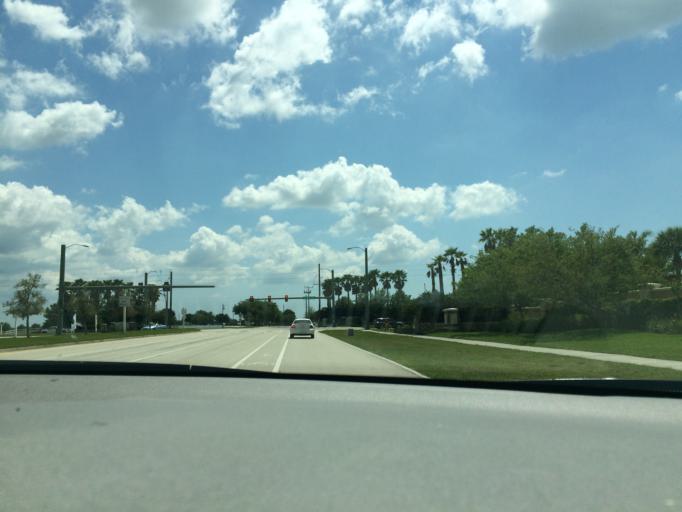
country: US
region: Florida
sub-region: Sarasota County
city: The Meadows
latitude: 27.3876
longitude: -82.3983
